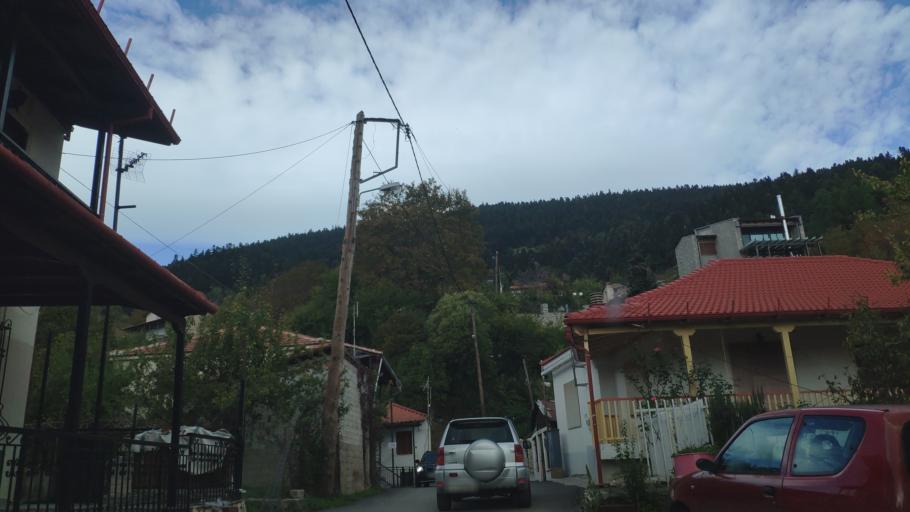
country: GR
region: Central Greece
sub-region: Nomos Fthiotidos
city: Stavros
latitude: 38.7405
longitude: 22.3371
